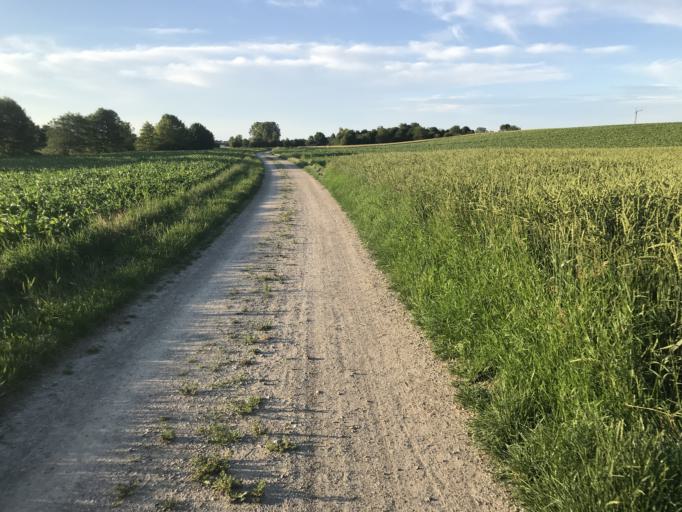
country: DE
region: Bavaria
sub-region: Swabia
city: Merching
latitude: 48.2536
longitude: 10.9665
